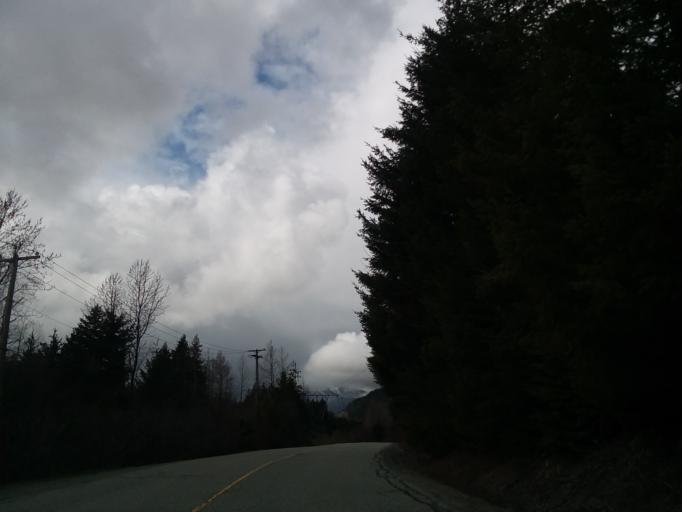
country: CA
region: British Columbia
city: Whistler
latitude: 50.0946
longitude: -123.0113
